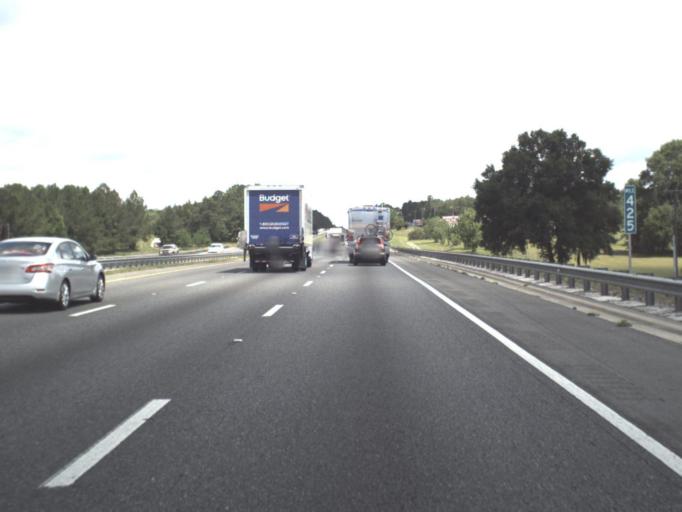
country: US
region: Florida
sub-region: Columbia County
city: Lake City
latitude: 30.1472
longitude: -82.6718
